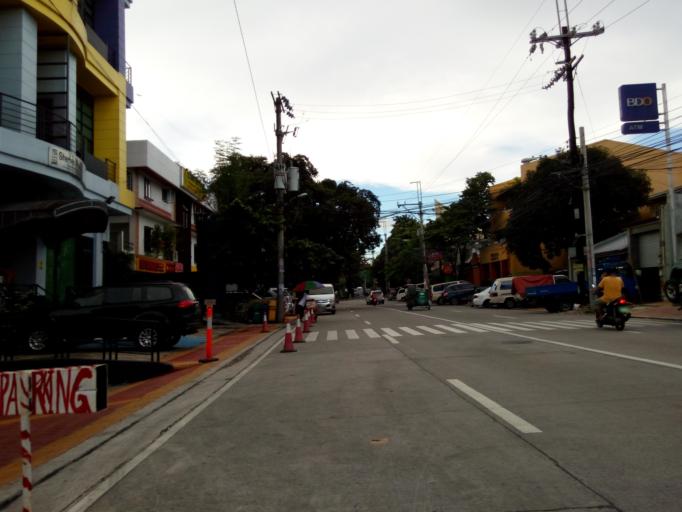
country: PH
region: Metro Manila
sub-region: Quezon City
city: Quezon City
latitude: 14.6448
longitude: 121.0609
